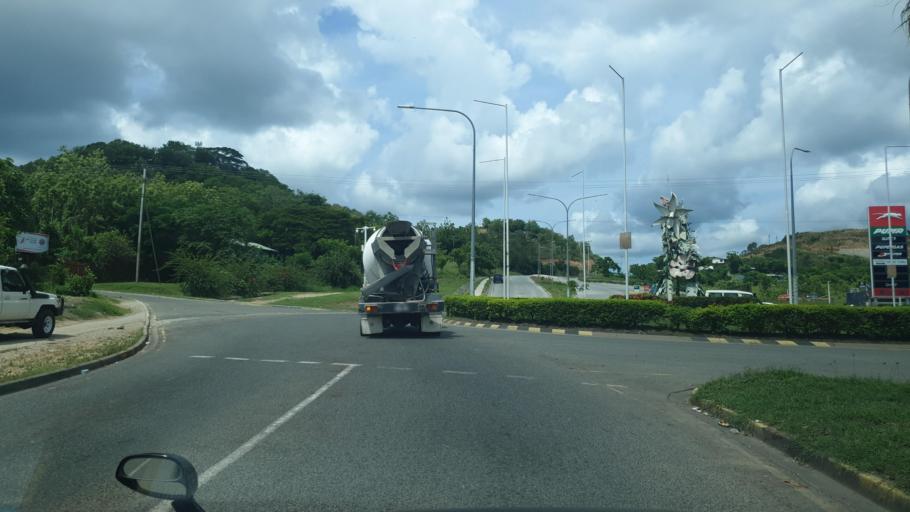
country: PG
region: National Capital
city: Port Moresby
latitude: -9.4088
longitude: 147.1650
